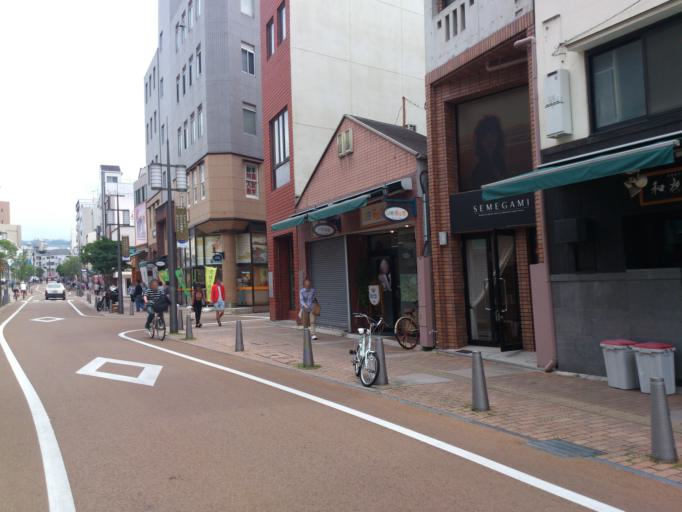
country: JP
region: Ehime
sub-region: Shikoku-chuo Shi
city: Matsuyama
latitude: 33.8430
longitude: 132.7709
